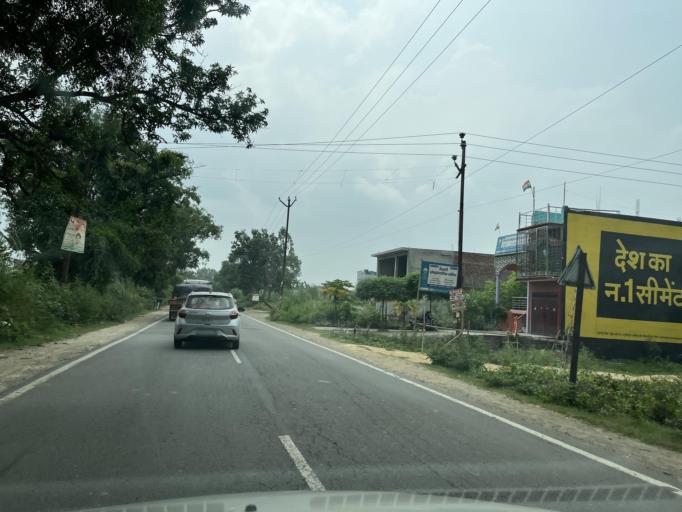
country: IN
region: Uttar Pradesh
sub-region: Bijnor
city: Najibabad
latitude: 29.5910
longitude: 78.3391
